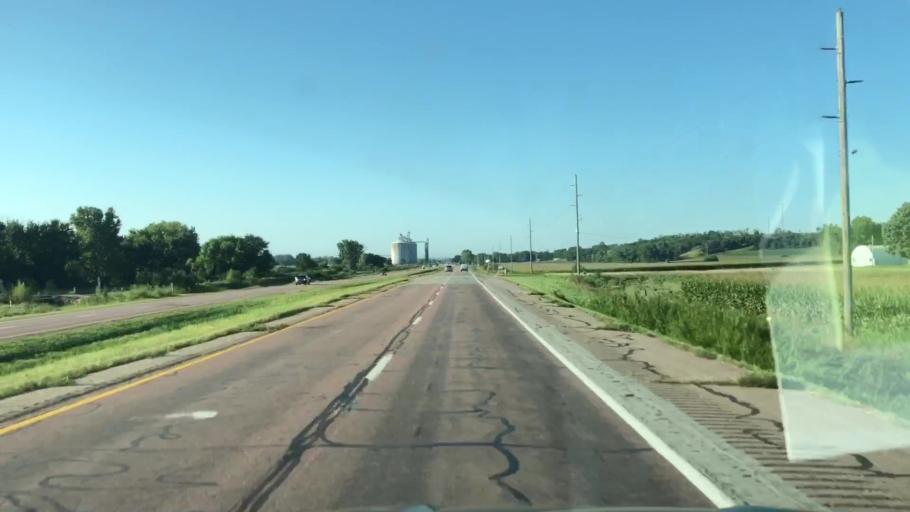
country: US
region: Iowa
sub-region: Woodbury County
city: Sioux City
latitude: 42.6429
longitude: -96.2879
